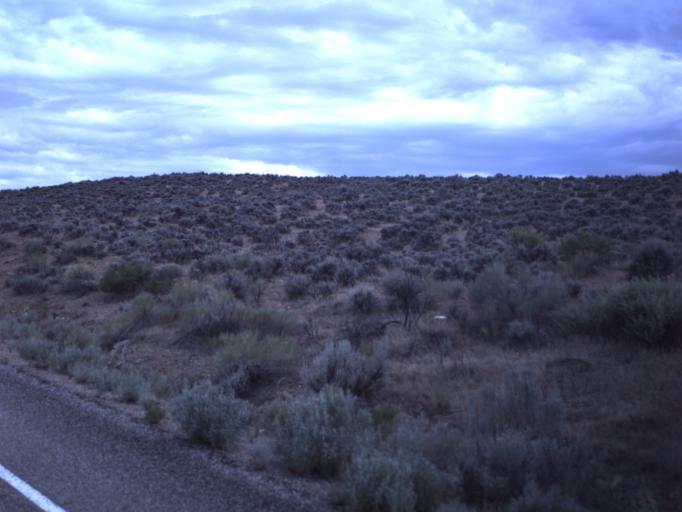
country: US
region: Colorado
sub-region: Rio Blanco County
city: Rangely
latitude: 39.9637
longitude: -109.1636
